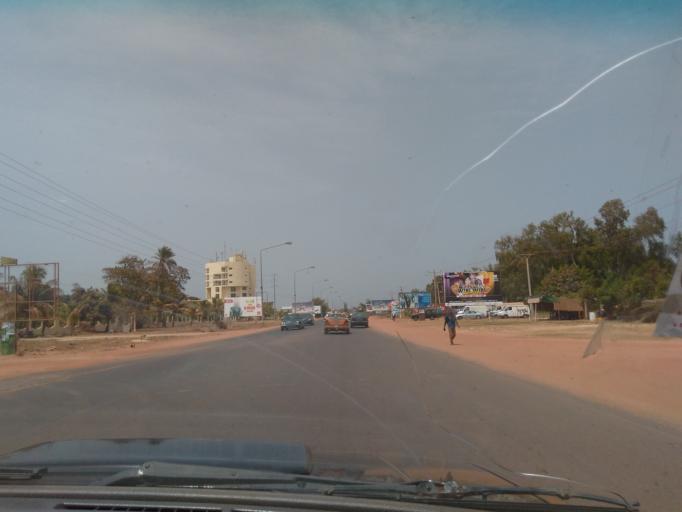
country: GM
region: Banjul
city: Bakau
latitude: 13.4564
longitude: -16.7041
